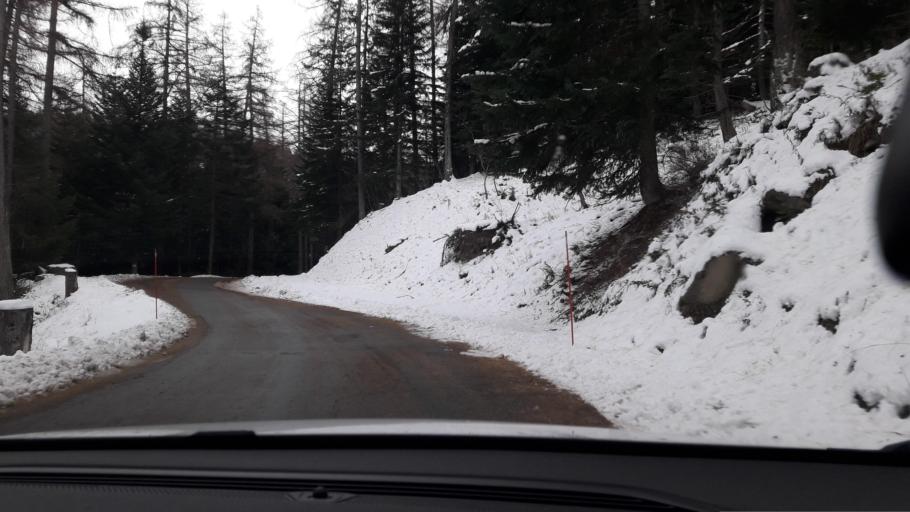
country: FR
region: Rhone-Alpes
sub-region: Departement de la Savoie
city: Saint-Michel-de-Maurienne
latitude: 45.2219
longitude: 6.4159
